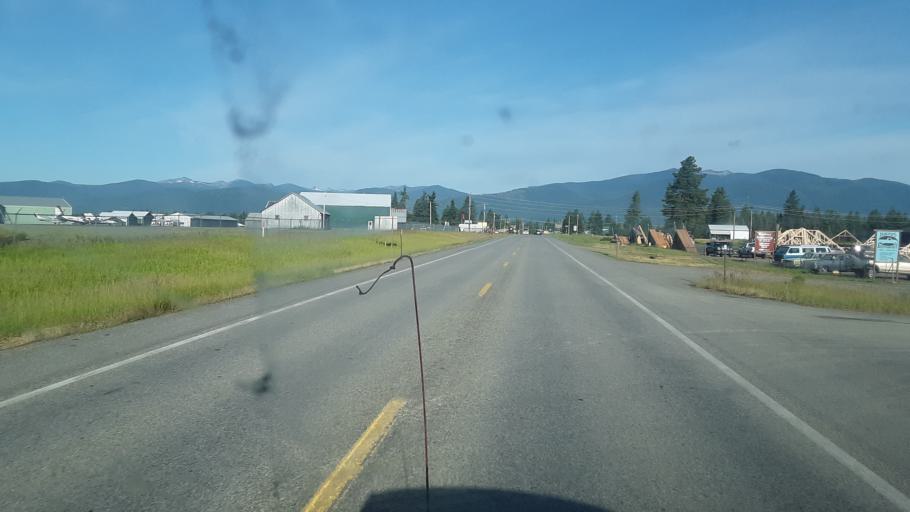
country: US
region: Idaho
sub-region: Boundary County
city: Bonners Ferry
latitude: 48.7314
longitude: -116.2893
